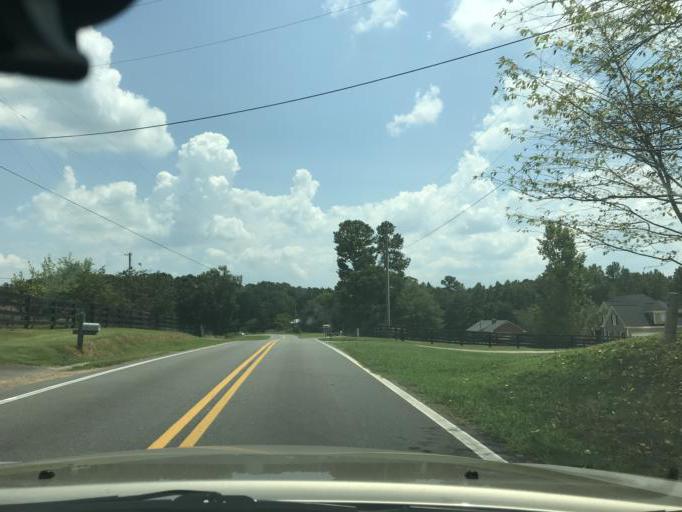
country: US
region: Georgia
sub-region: Forsyth County
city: Cumming
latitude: 34.2683
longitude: -84.2332
